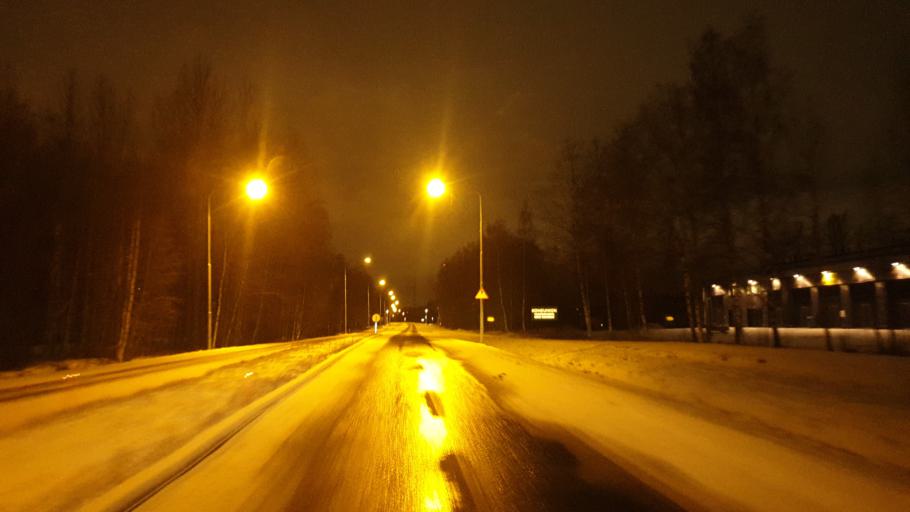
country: FI
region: Northern Ostrobothnia
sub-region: Oulu
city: Oulu
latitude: 64.9754
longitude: 25.4879
